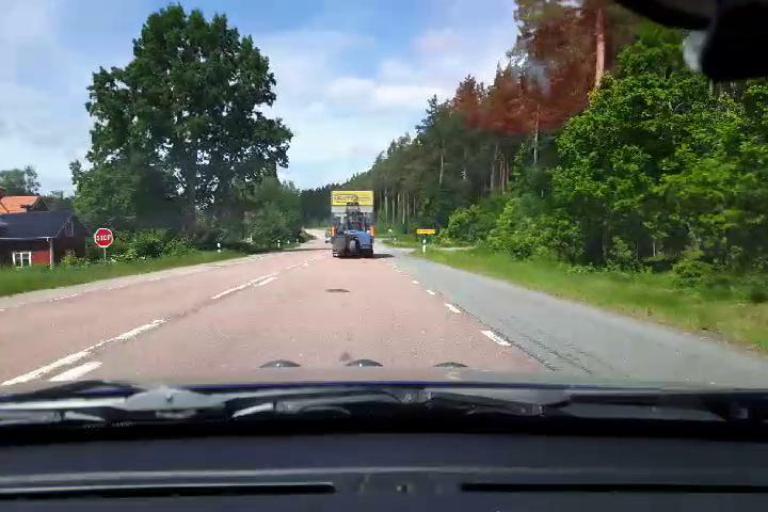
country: SE
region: Uppsala
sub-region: Osthammars Kommun
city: Bjorklinge
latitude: 60.1411
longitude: 17.5042
